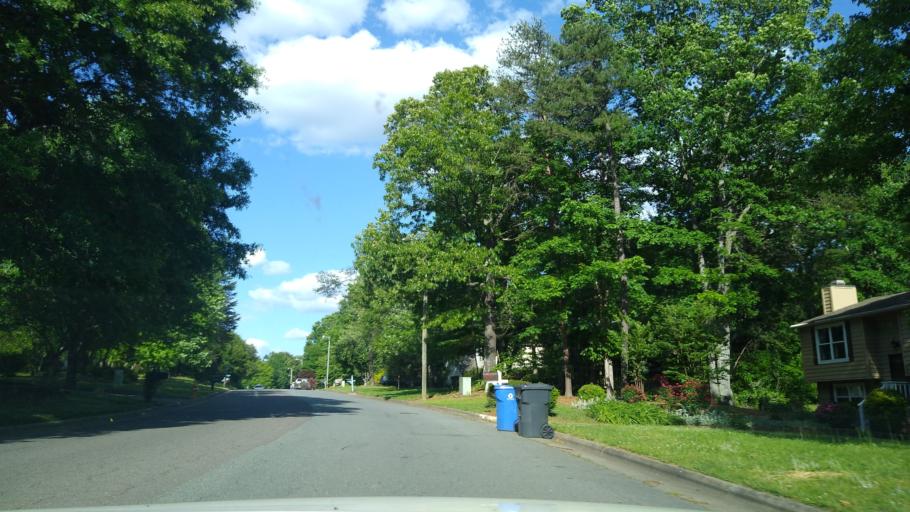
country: US
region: North Carolina
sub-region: Forsyth County
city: Kernersville
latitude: 36.1038
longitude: -80.0817
